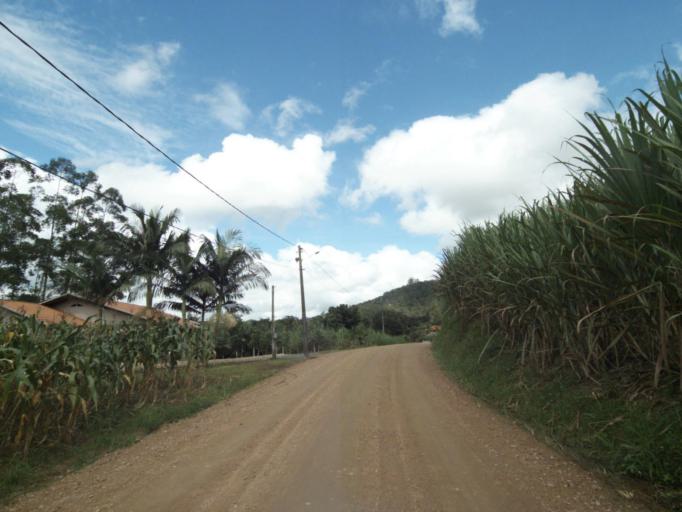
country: BR
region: Santa Catarina
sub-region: Pomerode
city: Pomerode
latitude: -26.6756
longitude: -49.1871
